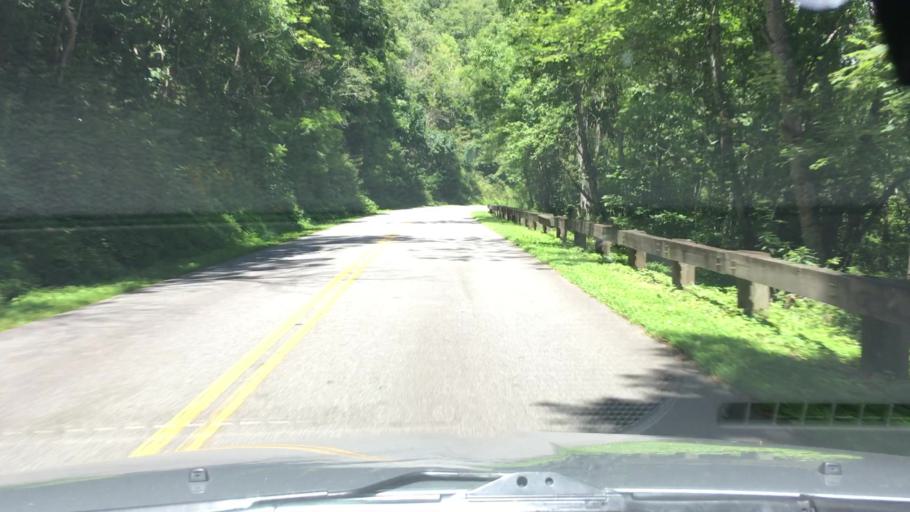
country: US
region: North Carolina
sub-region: Buncombe County
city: Asheville
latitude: 35.6499
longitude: -82.4864
